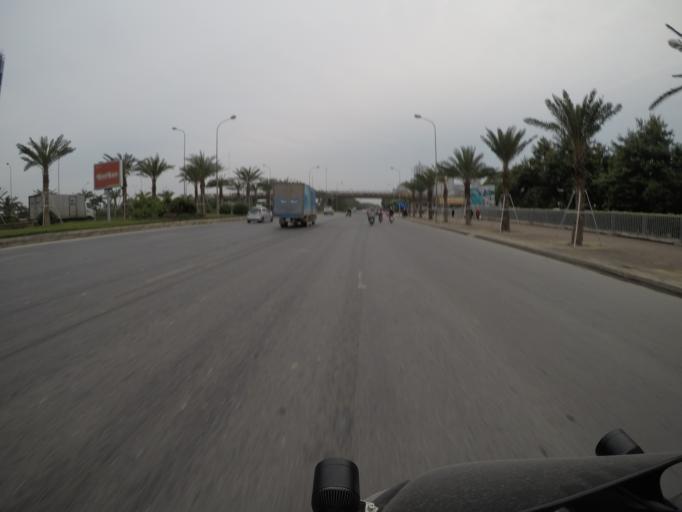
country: VN
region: Ha Noi
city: Thanh Xuan
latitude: 21.0026
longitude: 105.7835
